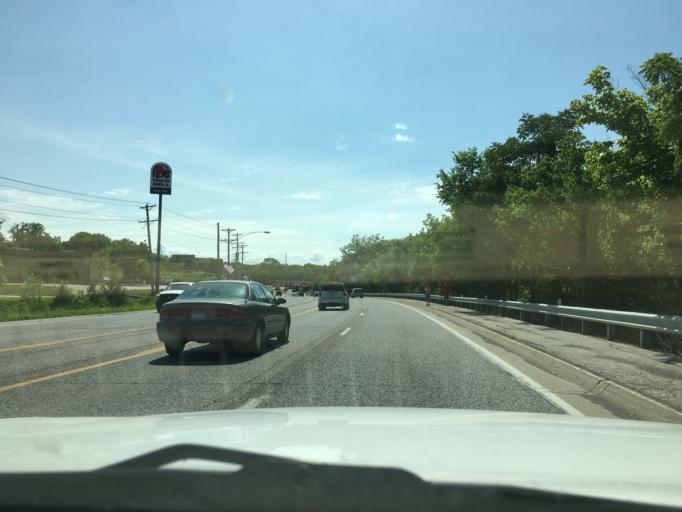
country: US
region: Missouri
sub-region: Franklin County
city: Union
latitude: 38.4443
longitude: -91.0013
